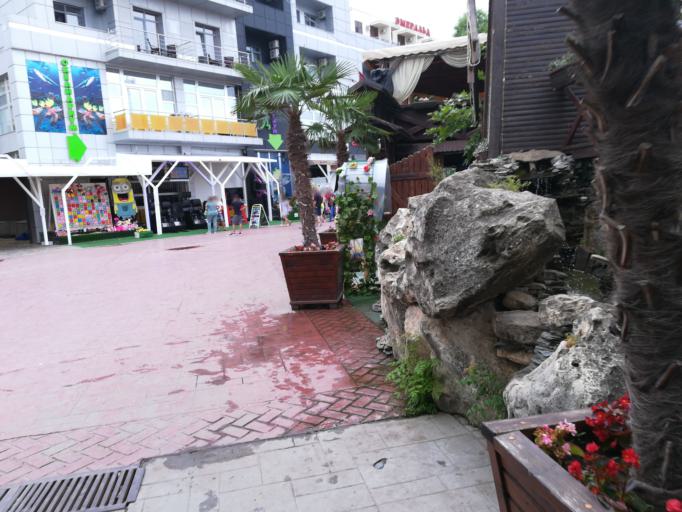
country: RU
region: Krasnodarskiy
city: Vityazevo
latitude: 44.9862
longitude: 37.2552
